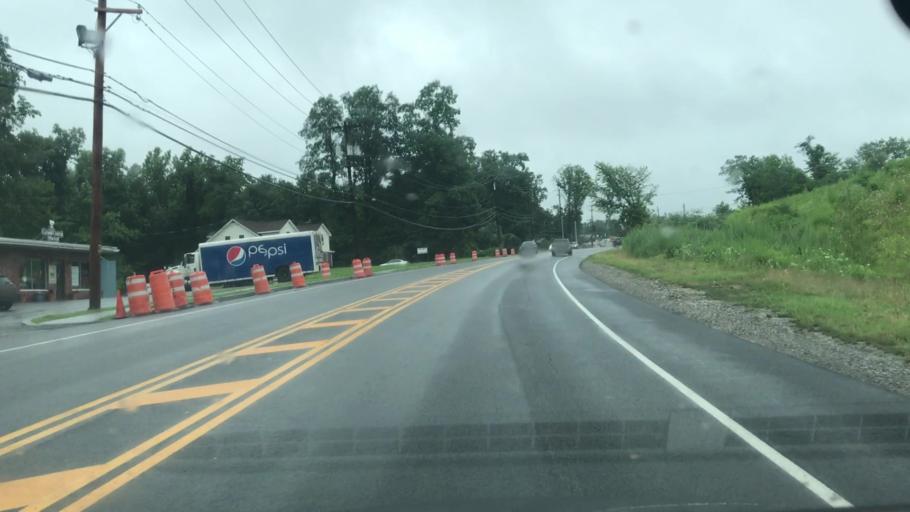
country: US
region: New York
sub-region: Westchester County
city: Shenorock
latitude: 41.3431
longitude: -73.7619
